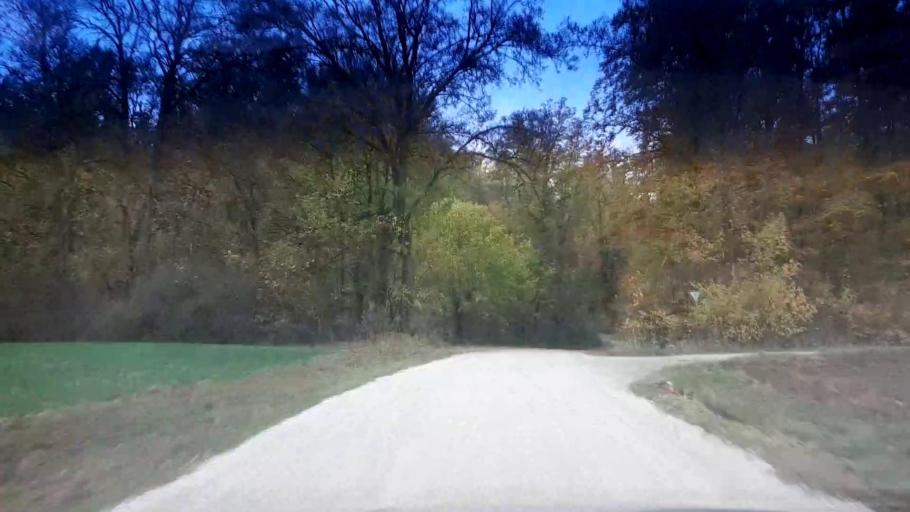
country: DE
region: Bavaria
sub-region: Upper Franconia
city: Schesslitz
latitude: 49.9648
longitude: 11.0319
